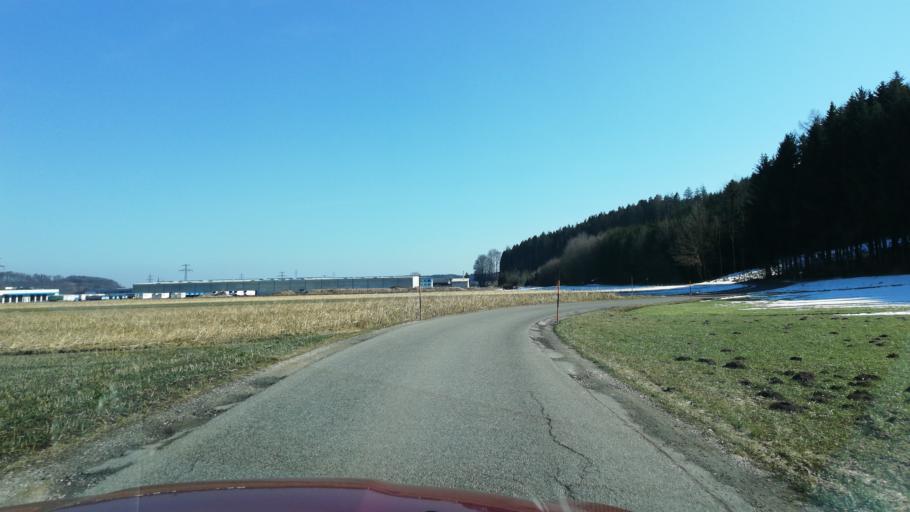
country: AT
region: Upper Austria
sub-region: Politischer Bezirk Vocklabruck
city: Vocklabruck
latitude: 47.9866
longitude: 13.6637
